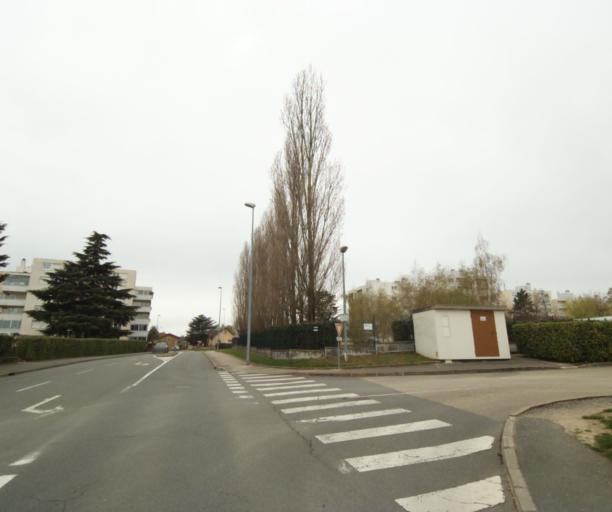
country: FR
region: Bourgogne
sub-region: Departement de Saone-et-Loire
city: Macon
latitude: 46.3110
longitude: 4.8117
